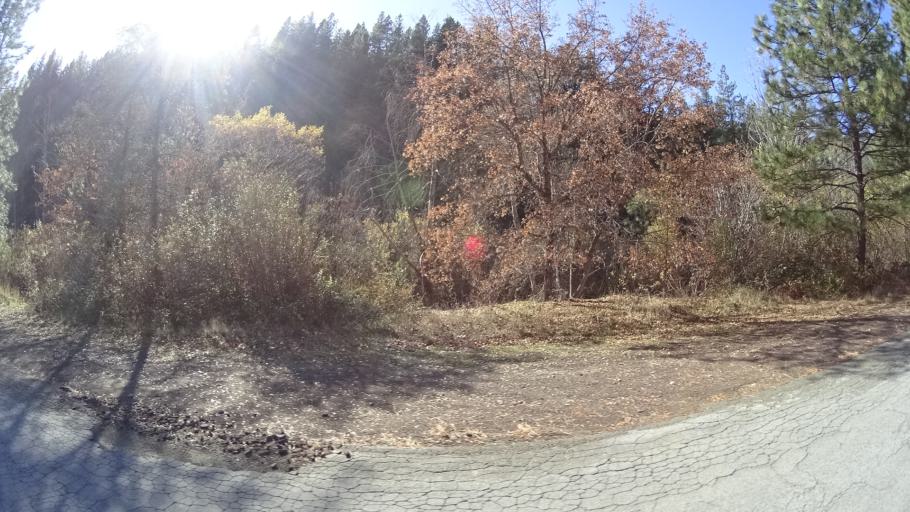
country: US
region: California
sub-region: Siskiyou County
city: Yreka
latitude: 41.7257
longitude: -122.7025
